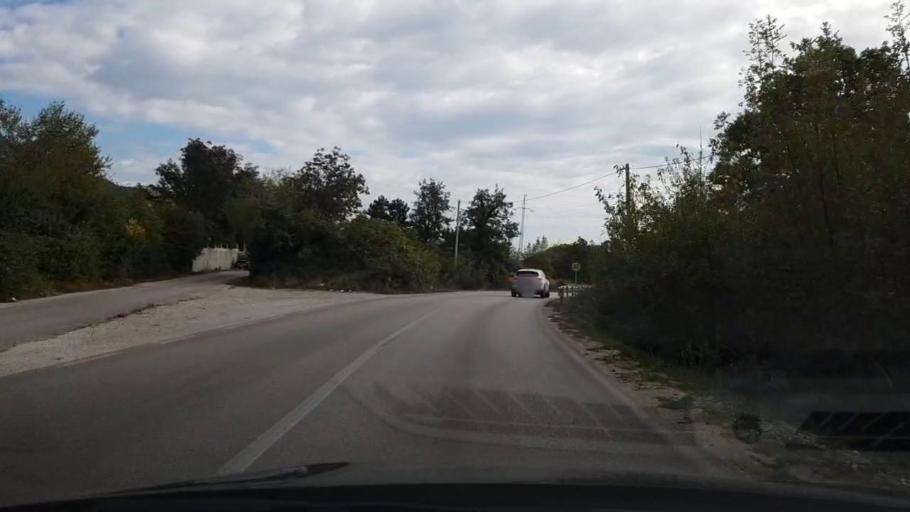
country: ME
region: Herceg Novi
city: Herceg-Novi
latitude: 42.4823
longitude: 18.5283
